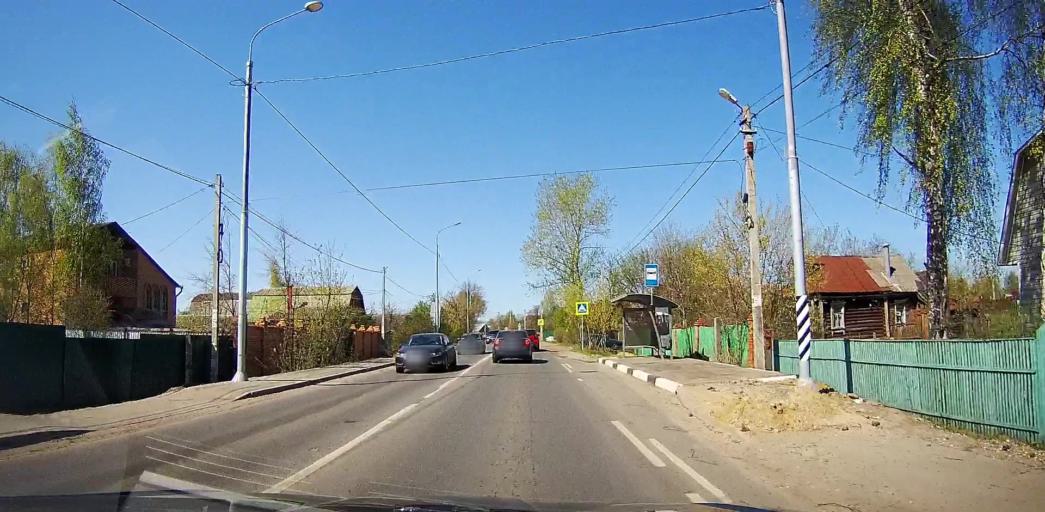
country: RU
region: Moskovskaya
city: Beloozerskiy
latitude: 55.4781
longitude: 38.4052
